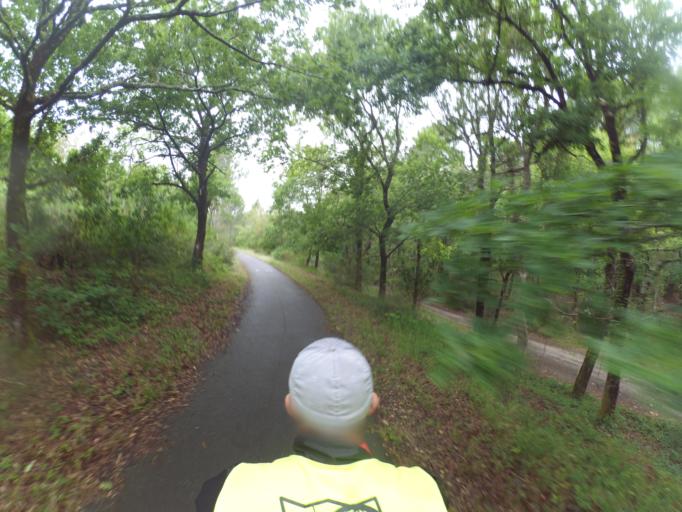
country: FR
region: Aquitaine
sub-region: Departement des Landes
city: Mimizan
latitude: 44.2179
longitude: -1.2352
